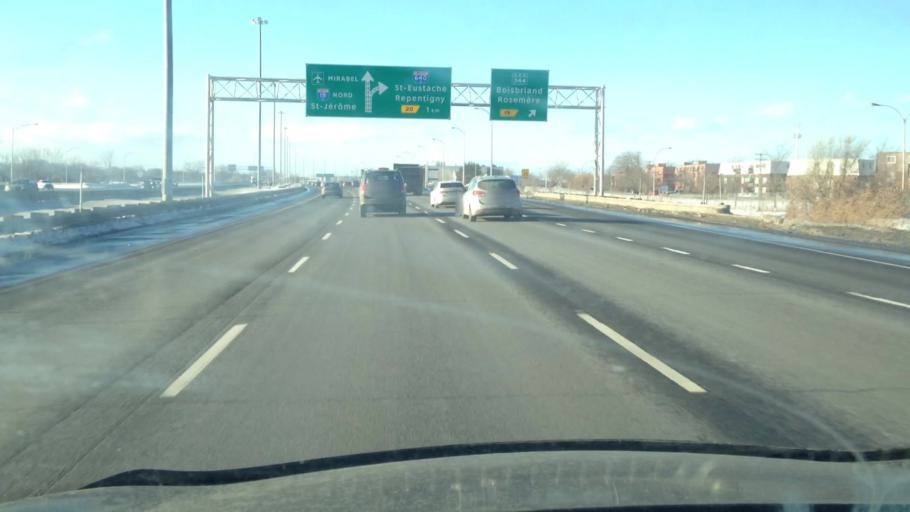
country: CA
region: Quebec
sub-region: Laurentides
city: Boisbriand
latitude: 45.6165
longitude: -73.8220
